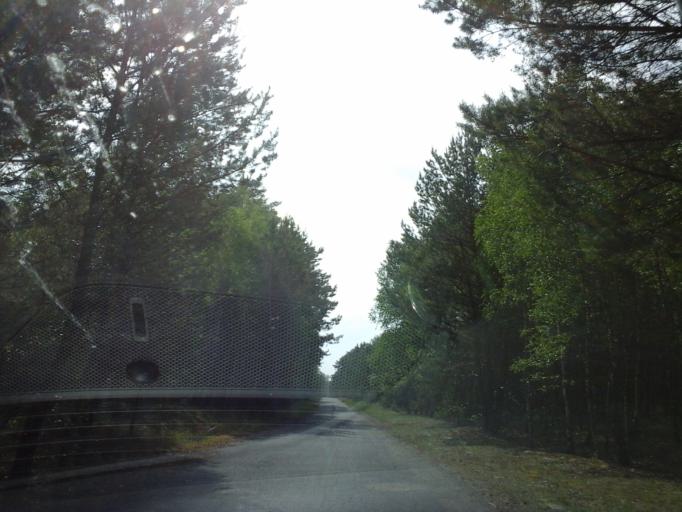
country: PL
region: West Pomeranian Voivodeship
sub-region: Powiat drawski
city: Kalisz Pomorski
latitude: 53.2071
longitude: 15.9557
